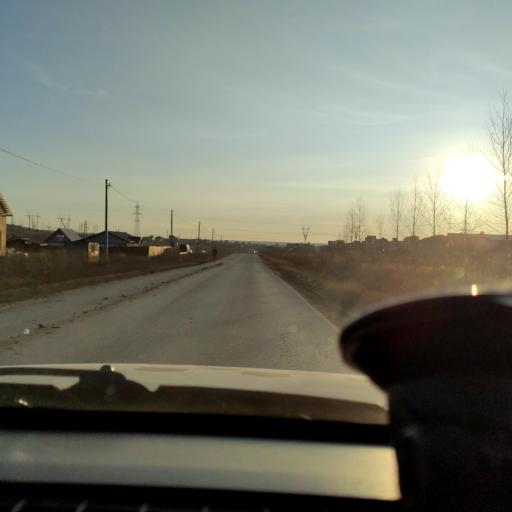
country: RU
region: Perm
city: Ferma
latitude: 57.9541
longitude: 56.3690
